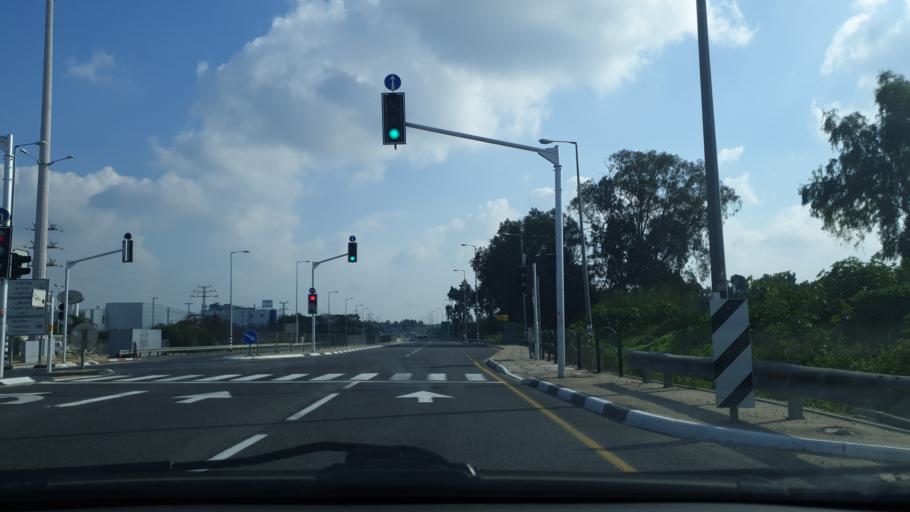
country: IL
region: Central District
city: Kefar Habad
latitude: 31.9639
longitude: 34.8484
